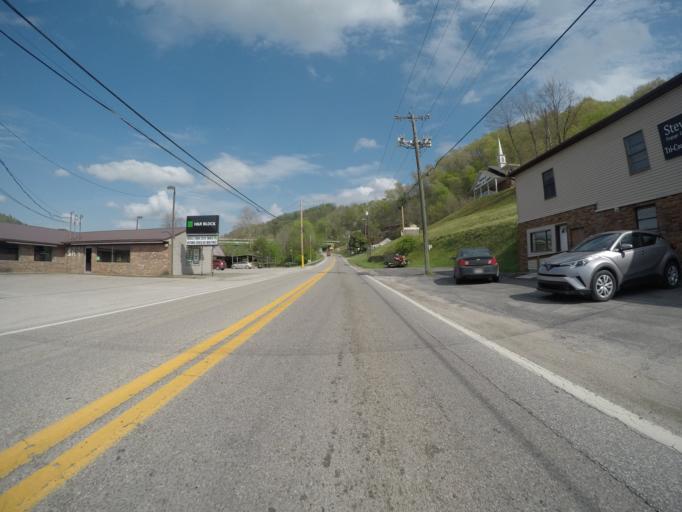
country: US
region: West Virginia
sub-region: Boone County
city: Madison
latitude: 38.0837
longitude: -81.8360
